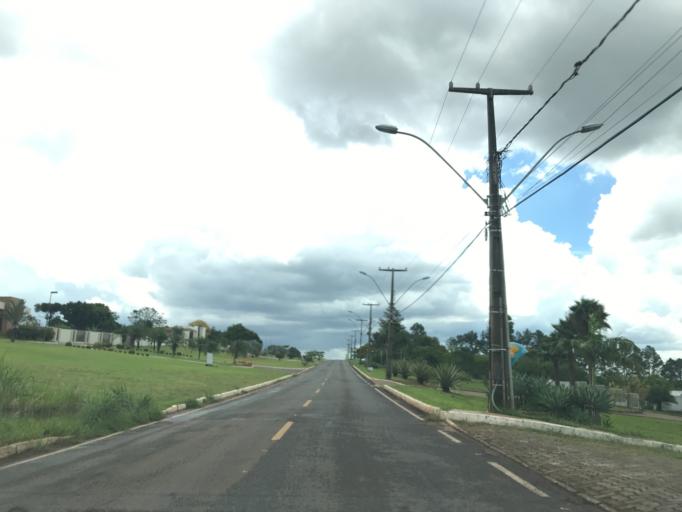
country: BR
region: Federal District
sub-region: Brasilia
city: Brasilia
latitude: -15.8976
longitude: -47.9131
